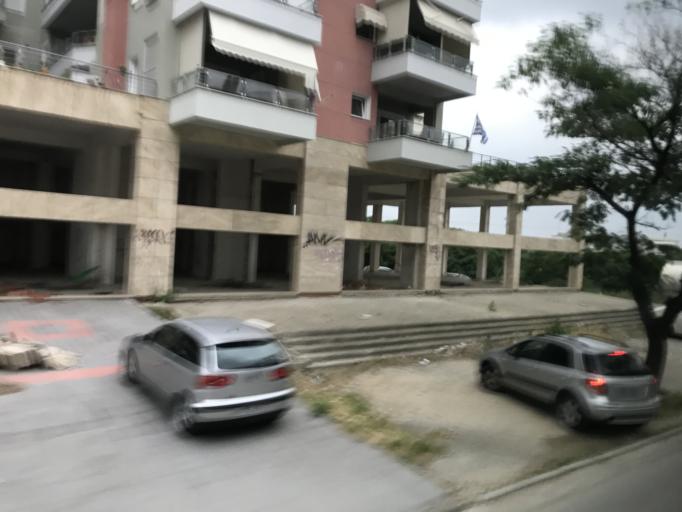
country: GR
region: East Macedonia and Thrace
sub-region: Nomos Xanthis
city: Xanthi
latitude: 41.1401
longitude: 24.8971
